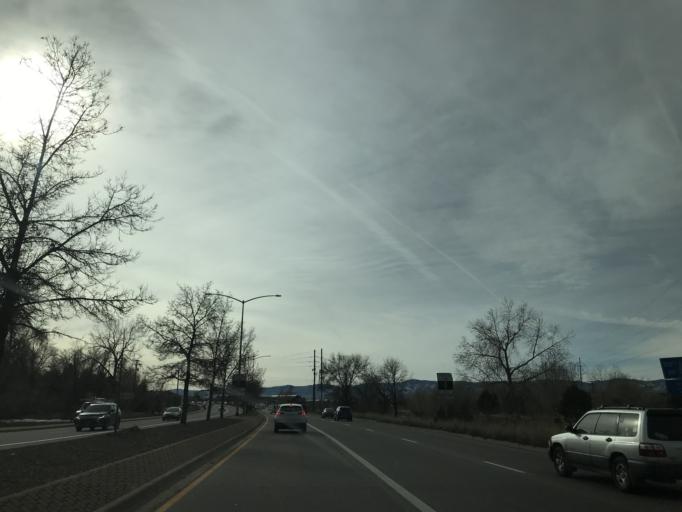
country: US
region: Colorado
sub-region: Arapahoe County
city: Littleton
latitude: 39.6182
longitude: -105.0184
